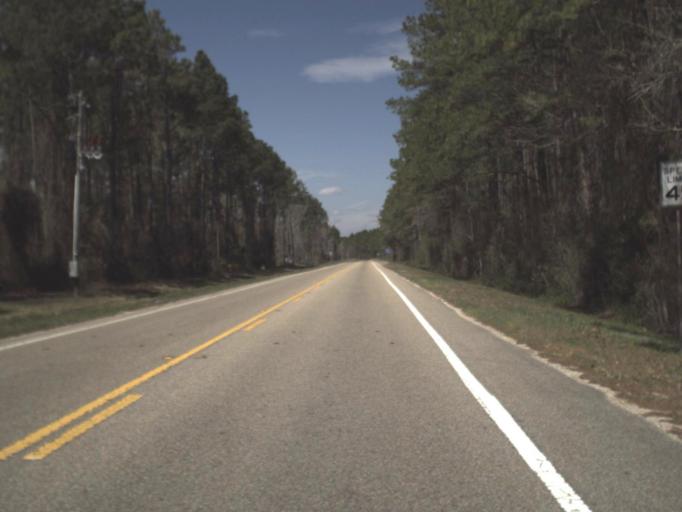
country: US
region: Florida
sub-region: Leon County
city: Woodville
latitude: 30.2015
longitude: -84.1853
